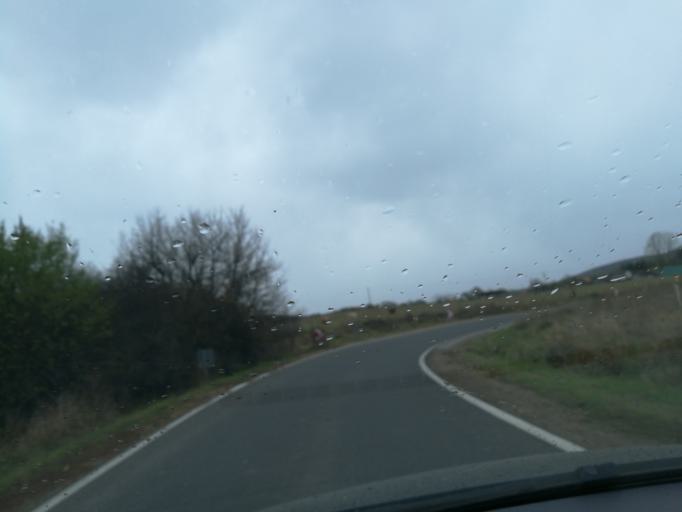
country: HU
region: Nograd
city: Paszto
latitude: 47.9771
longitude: 19.6324
